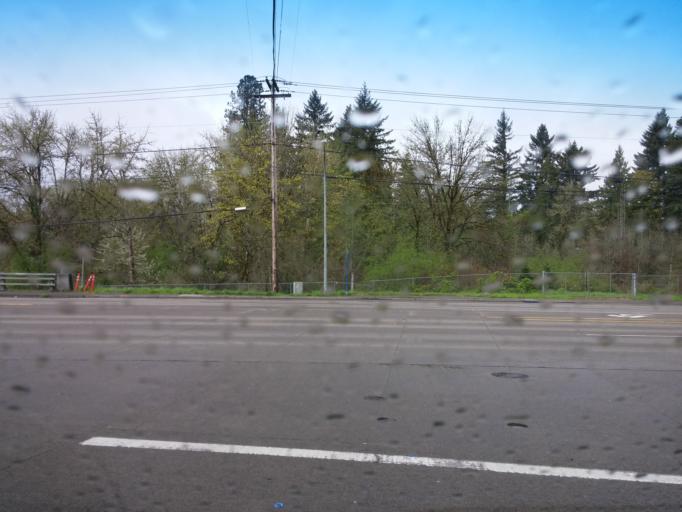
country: US
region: Oregon
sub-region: Washington County
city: Aloha
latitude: 45.5074
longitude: -122.8671
